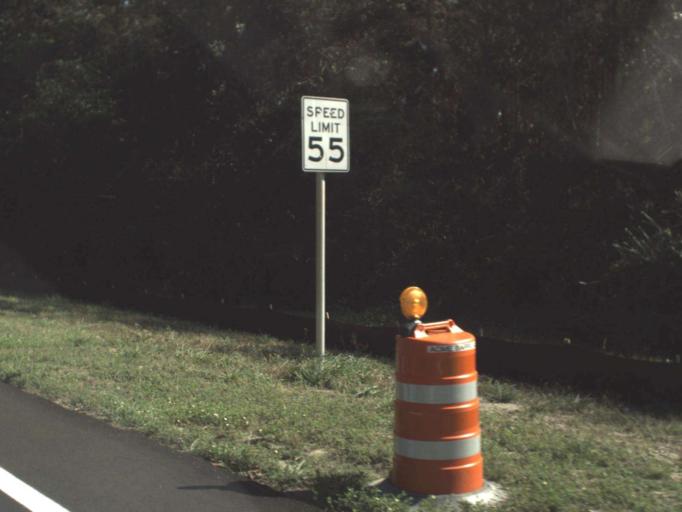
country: US
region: Florida
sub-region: Gulf County
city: Port Saint Joe
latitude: 29.7765
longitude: -85.2770
